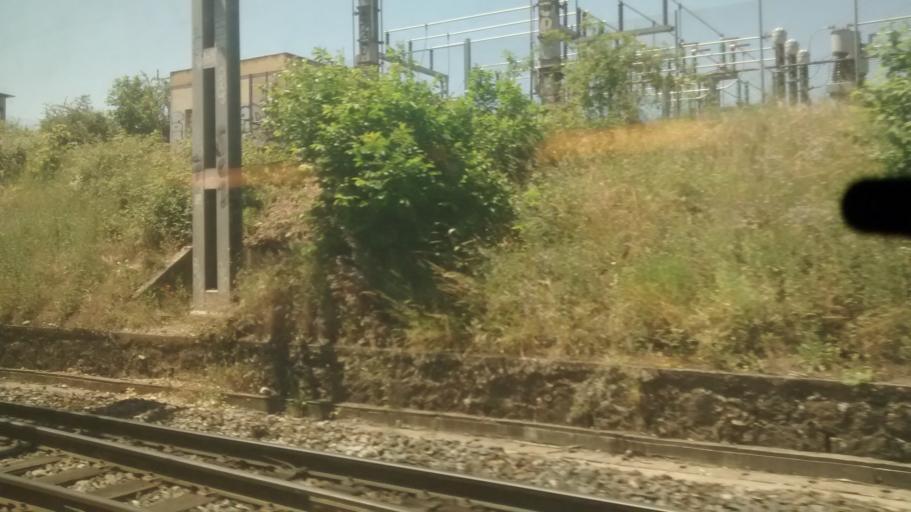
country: FR
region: Rhone-Alpes
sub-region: Departement du Rhone
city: Sathonay-Camp
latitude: 45.8153
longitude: 4.8697
